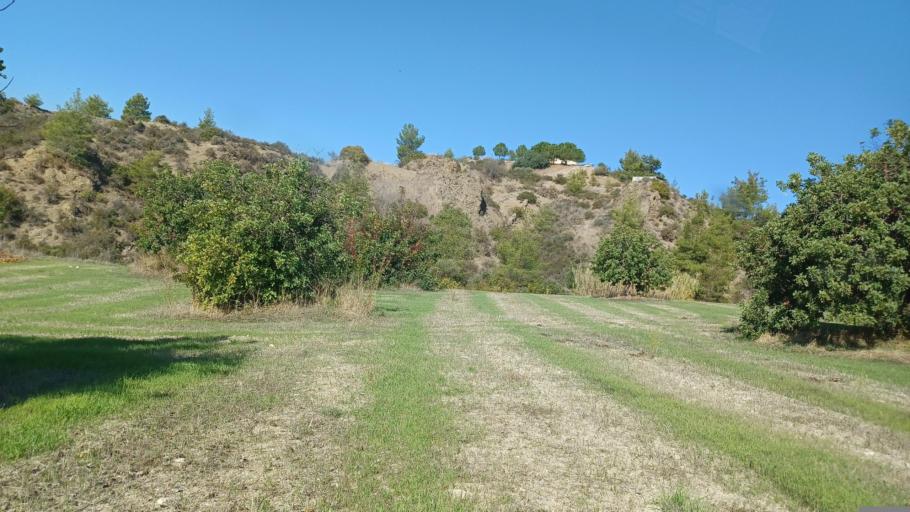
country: CY
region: Pafos
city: Polis
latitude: 35.0317
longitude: 32.4959
